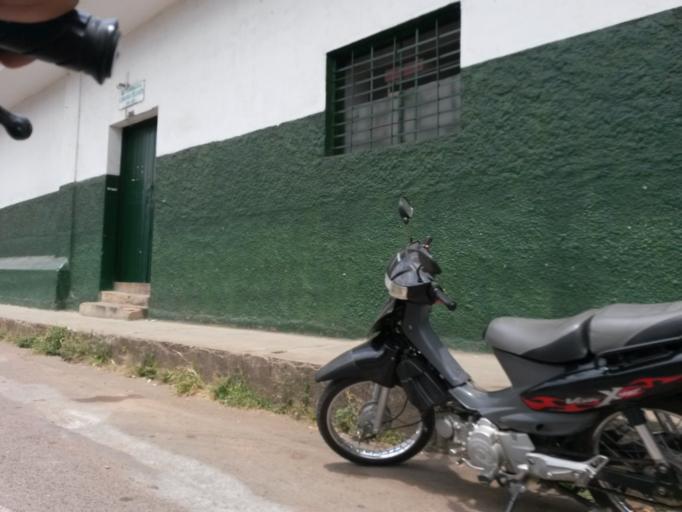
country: CO
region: Cauca
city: Santander de Quilichao
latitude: 3.0069
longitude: -76.4820
